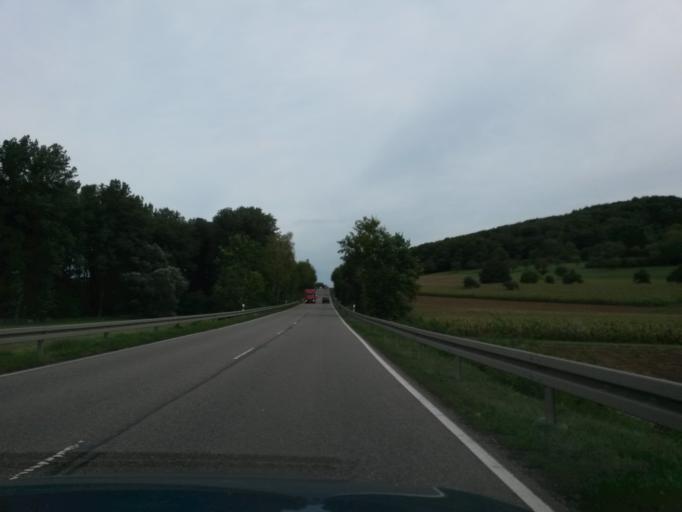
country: DE
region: Baden-Wuerttemberg
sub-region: Karlsruhe Region
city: Konigsbach-Stein
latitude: 48.9563
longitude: 8.5890
